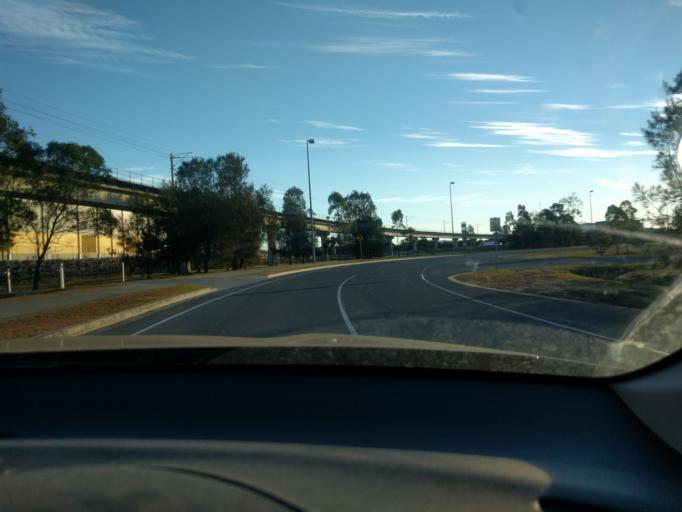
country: AU
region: Queensland
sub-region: Brisbane
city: Ascot
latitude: -27.4150
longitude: 153.0889
